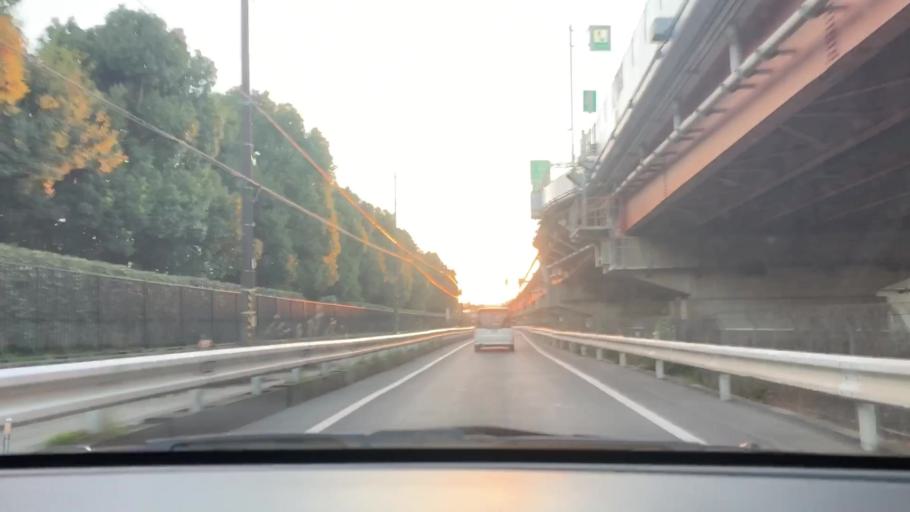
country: JP
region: Saitama
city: Yashio-shi
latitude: 35.8407
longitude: 139.8665
